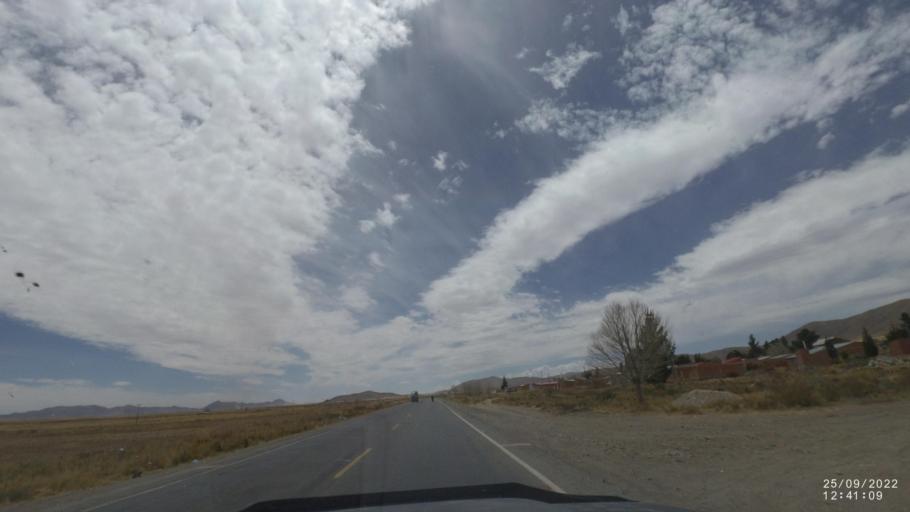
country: BO
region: Oruro
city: Machacamarca
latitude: -18.1079
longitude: -67.0059
